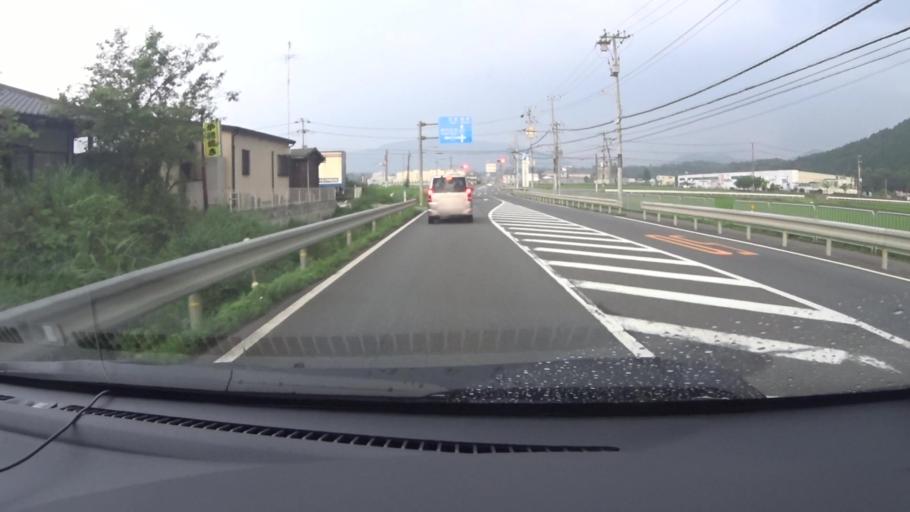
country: JP
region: Kyoto
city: Ayabe
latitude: 35.1841
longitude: 135.4184
